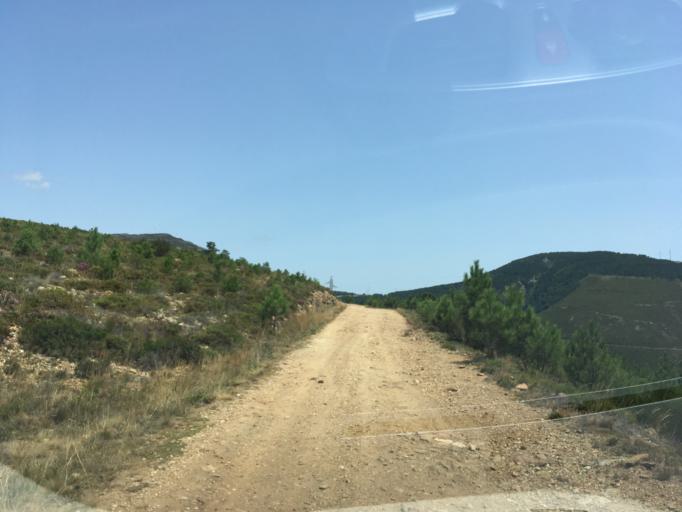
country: PT
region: Porto
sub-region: Baiao
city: Valadares
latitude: 41.2708
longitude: -7.9473
